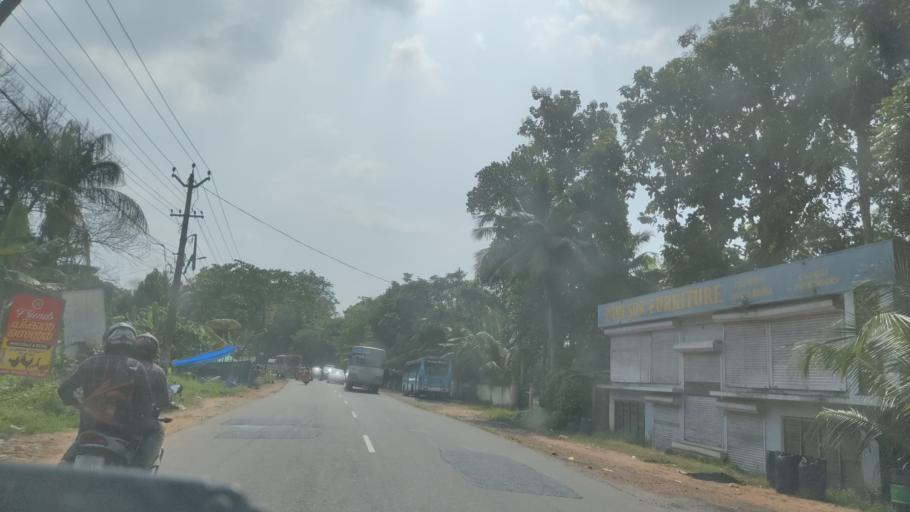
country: IN
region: Kerala
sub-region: Pattanamtitta
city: Tiruvalla
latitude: 9.3333
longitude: 76.5331
